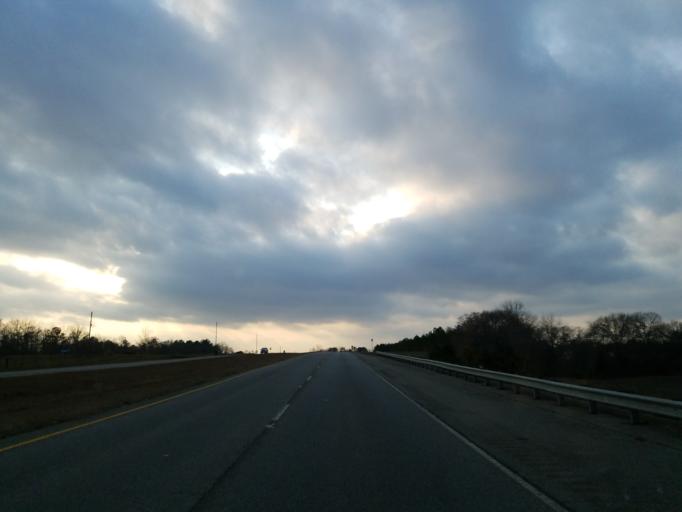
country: US
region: Georgia
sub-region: Bartow County
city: Euharlee
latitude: 34.0969
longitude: -84.9455
